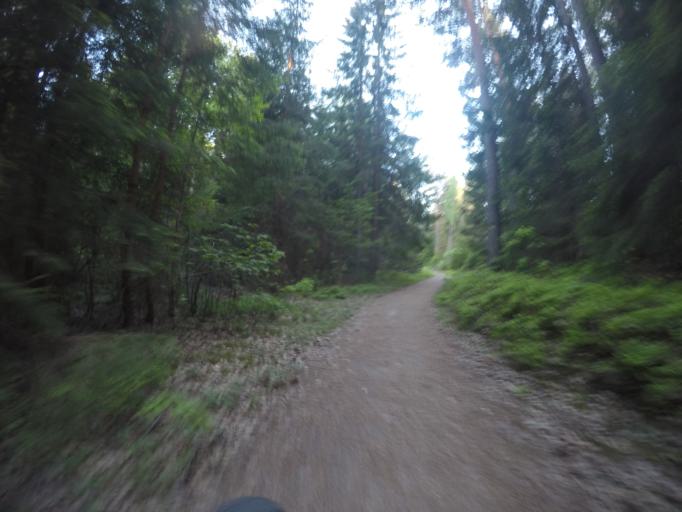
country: SE
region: Soedermanland
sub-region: Eskilstuna Kommun
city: Skogstorp
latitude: 59.3395
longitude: 16.5043
